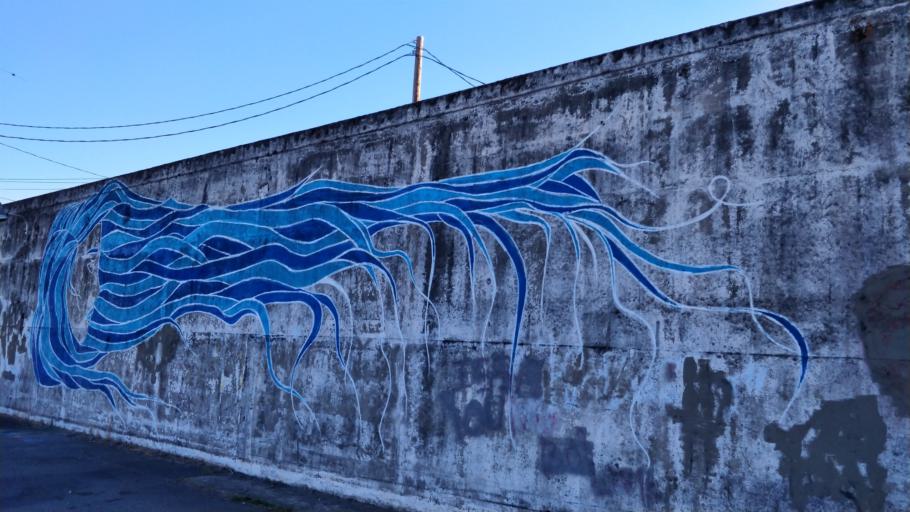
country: US
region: California
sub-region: Shasta County
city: Redding
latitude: 40.5729
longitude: -122.3875
